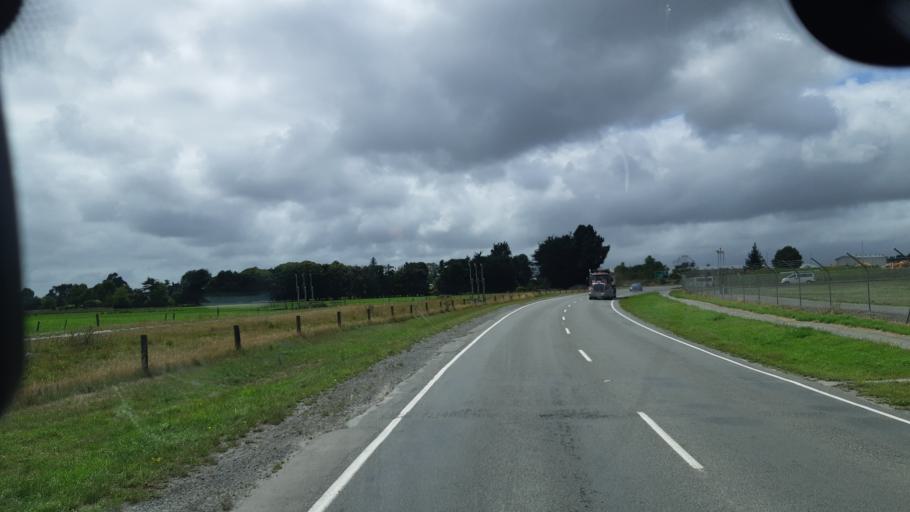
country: NZ
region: Canterbury
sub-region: Christchurch City
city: Christchurch
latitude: -43.4686
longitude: 172.5537
